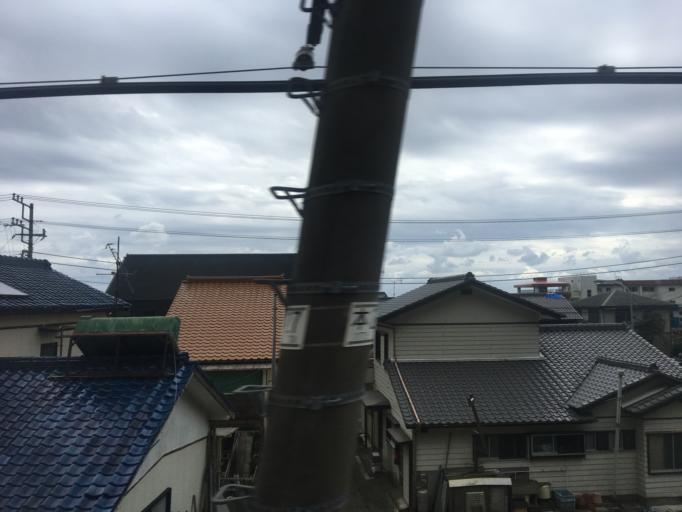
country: JP
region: Chiba
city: Kawaguchi
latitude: 35.1251
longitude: 140.1659
